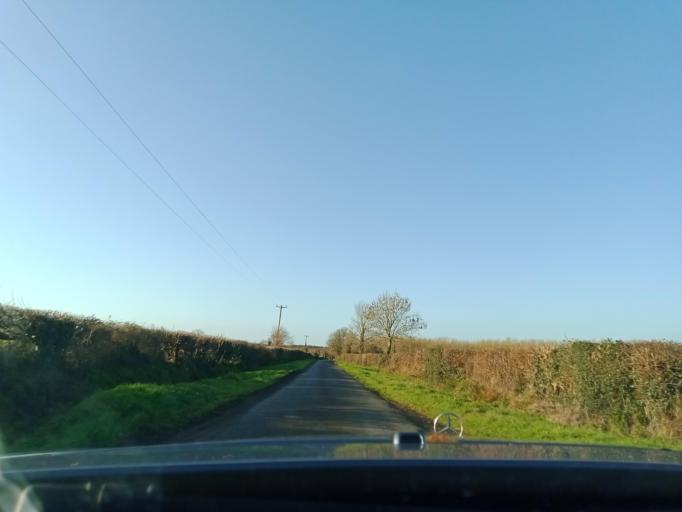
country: IE
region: Leinster
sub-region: Kilkenny
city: Callan
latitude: 52.5004
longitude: -7.4027
